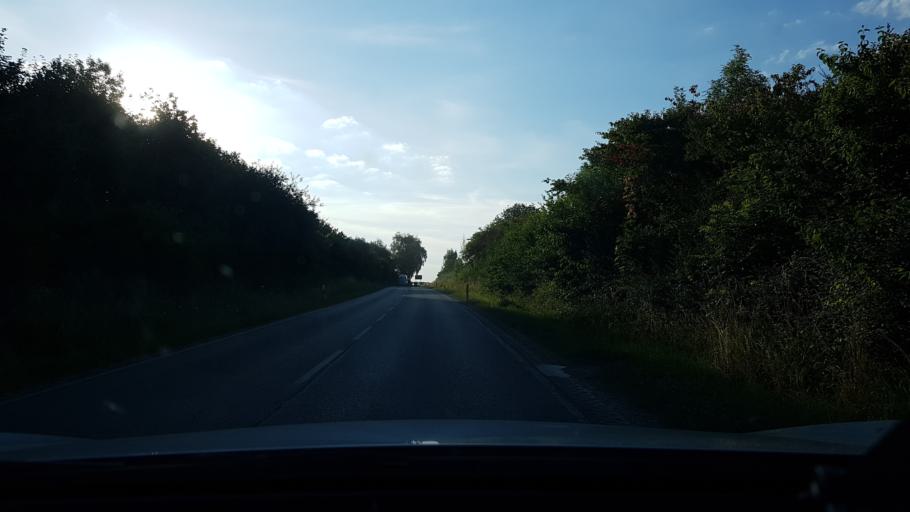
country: DE
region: Baden-Wuerttemberg
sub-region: Tuebingen Region
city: Warthausen
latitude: 48.1565
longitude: 9.8368
